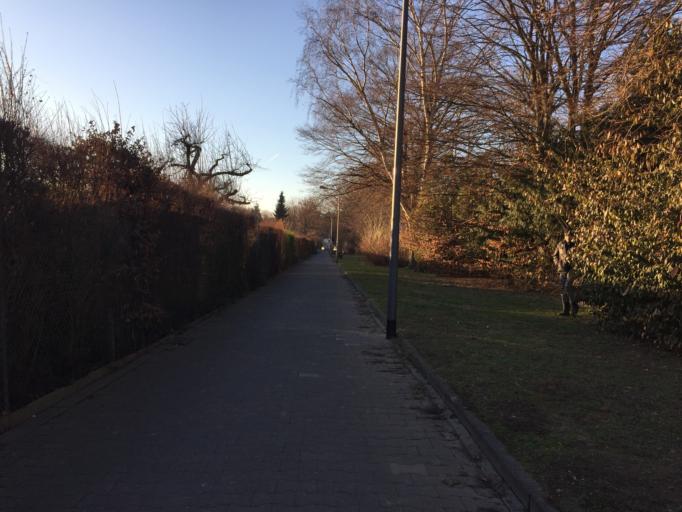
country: DE
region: Hesse
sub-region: Regierungsbezirk Darmstadt
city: Frankfurt am Main
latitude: 50.1577
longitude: 8.6654
